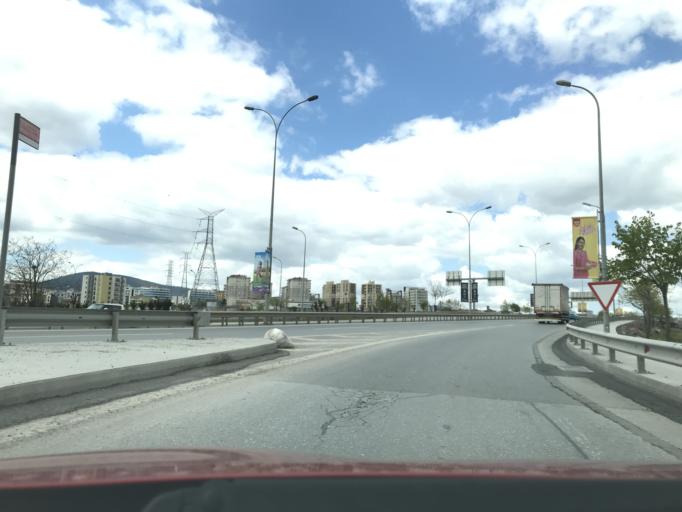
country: TR
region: Istanbul
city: Pendik
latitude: 40.9149
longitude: 29.3127
